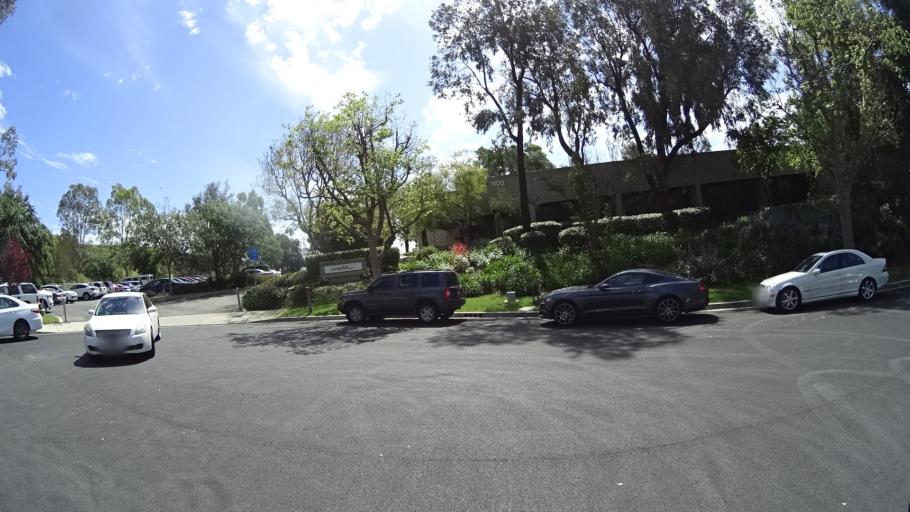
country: US
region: California
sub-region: Ventura County
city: Casa Conejo
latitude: 34.1942
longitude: -118.9424
